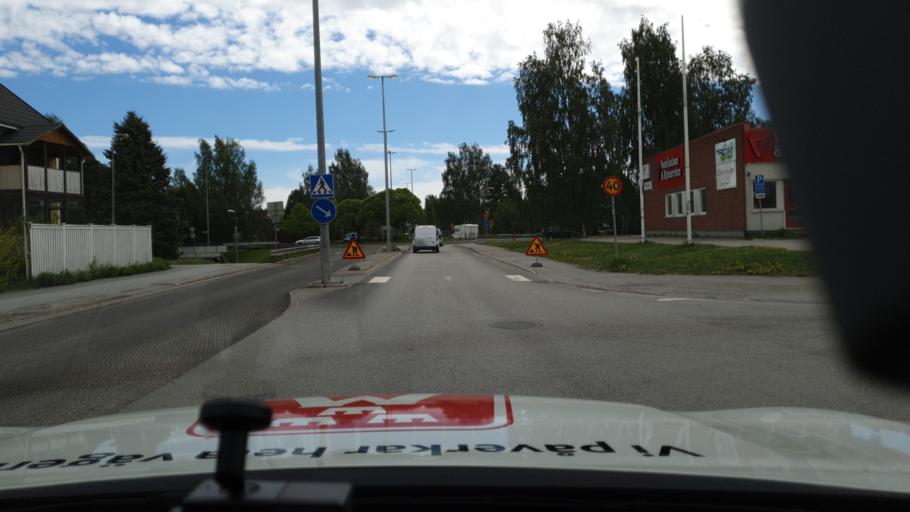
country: SE
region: Vaesterbotten
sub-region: Umea Kommun
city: Umea
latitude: 63.8179
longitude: 20.2567
